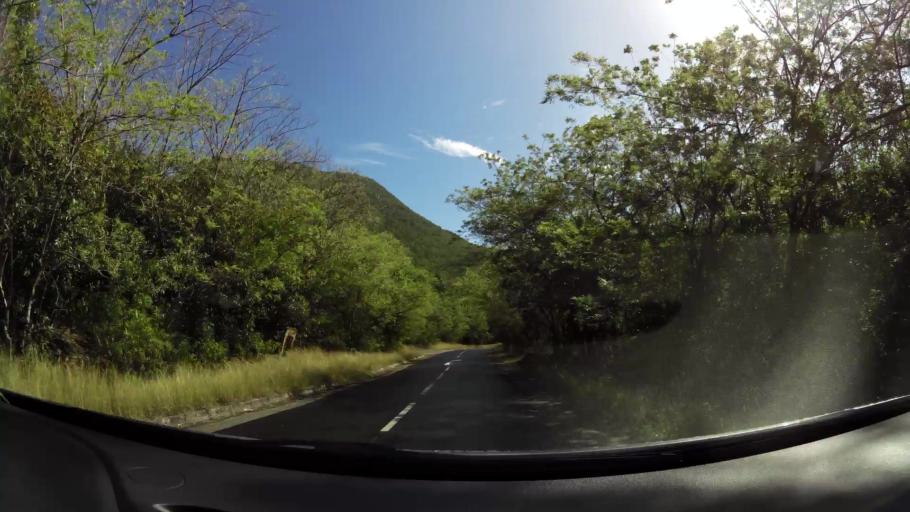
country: MQ
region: Martinique
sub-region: Martinique
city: Les Trois-Ilets
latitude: 14.4592
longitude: -61.0645
